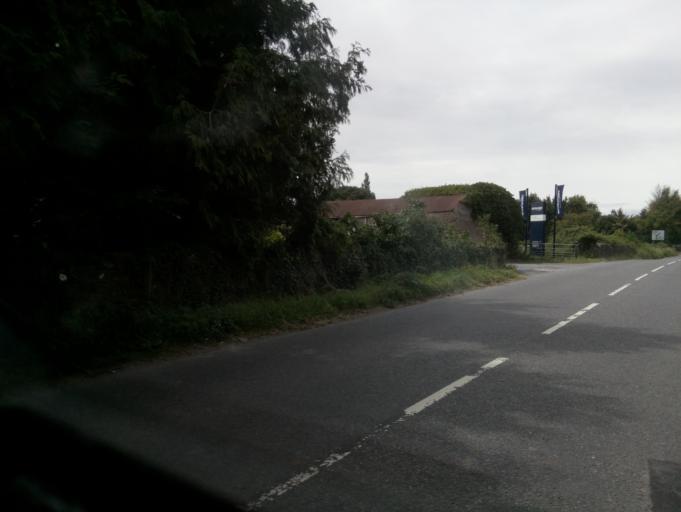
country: GB
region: England
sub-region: North Somerset
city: Yatton
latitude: 51.4001
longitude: -2.8387
